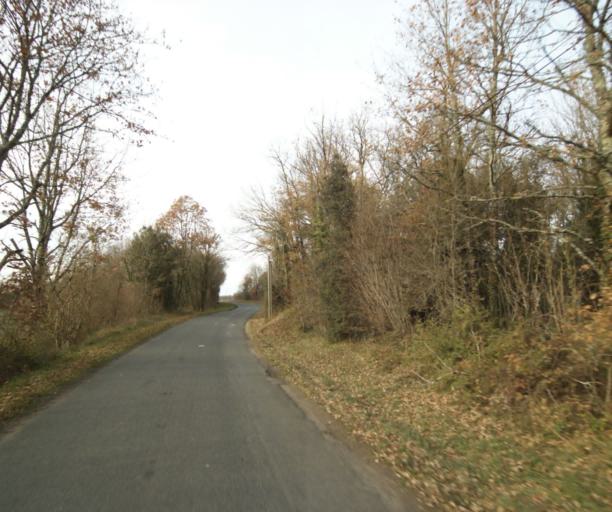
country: FR
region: Poitou-Charentes
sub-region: Departement de la Charente-Maritime
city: Saint-Hilaire-de-Villefranche
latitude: 45.8195
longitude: -0.5596
